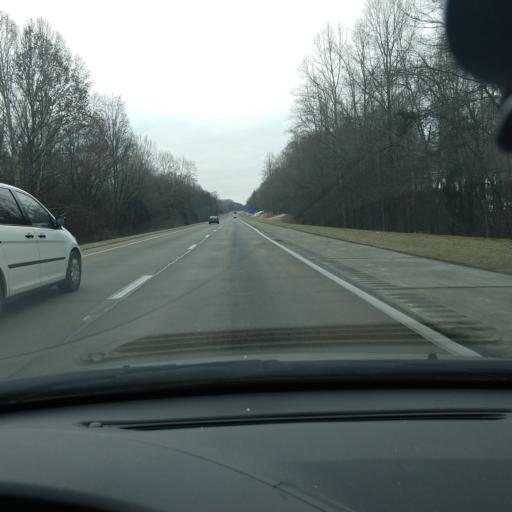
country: US
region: North Carolina
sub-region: Davidson County
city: Midway
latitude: 35.9839
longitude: -80.2352
